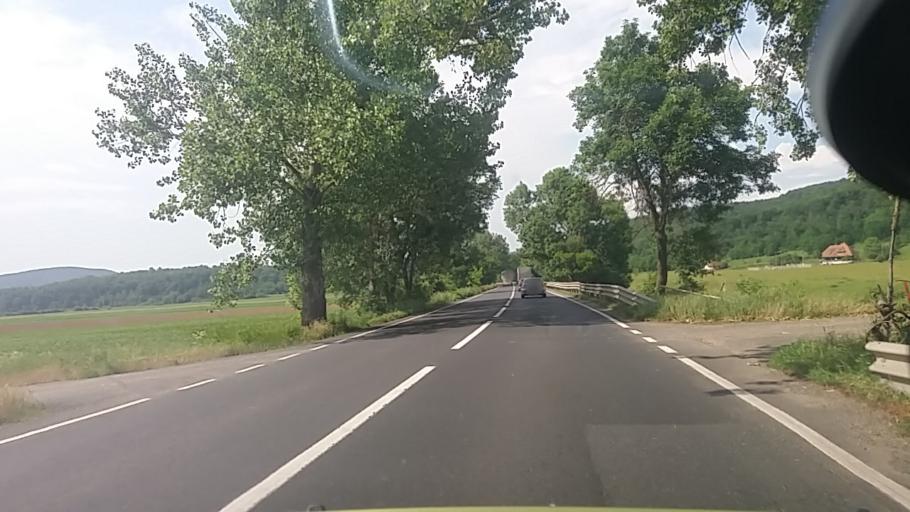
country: RO
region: Arad
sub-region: Comuna Varadia de Mures
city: Varadia de Mures
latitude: 46.0153
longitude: 22.1495
